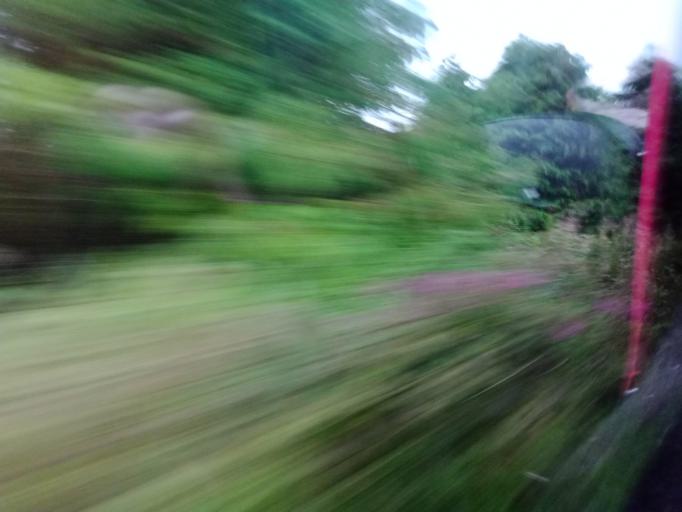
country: IE
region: Munster
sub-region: Waterford
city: Dungarvan
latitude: 52.0481
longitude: -7.6536
